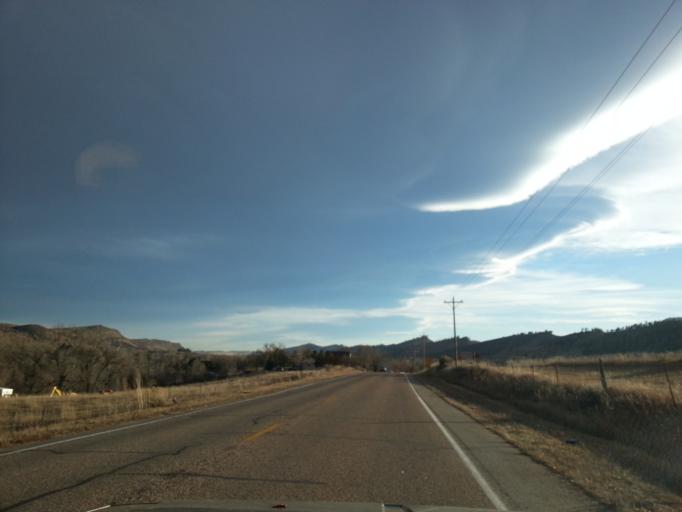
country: US
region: Colorado
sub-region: Larimer County
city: Laporte
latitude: 40.4856
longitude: -105.2110
